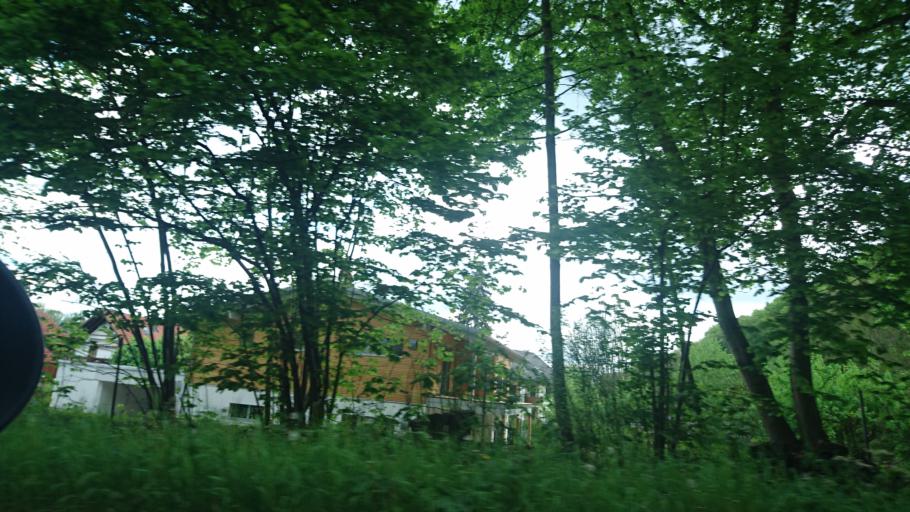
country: DE
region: Bavaria
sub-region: Lower Bavaria
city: Ergolding
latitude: 48.5507
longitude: 12.1955
